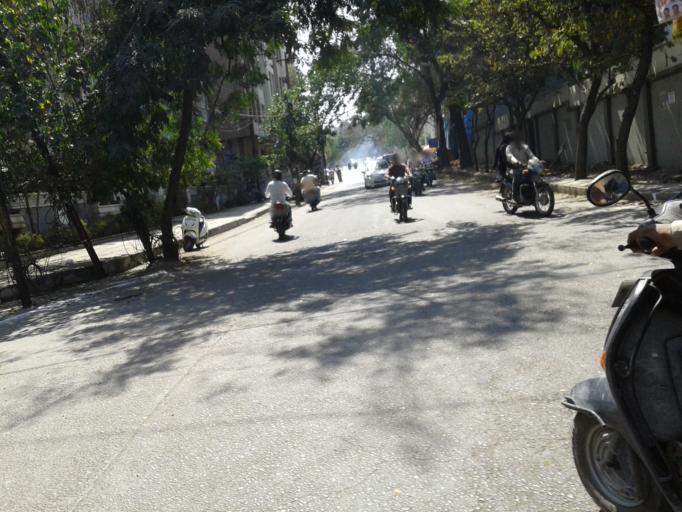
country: IN
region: Telangana
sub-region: Hyderabad
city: Hyderabad
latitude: 17.4294
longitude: 78.4394
